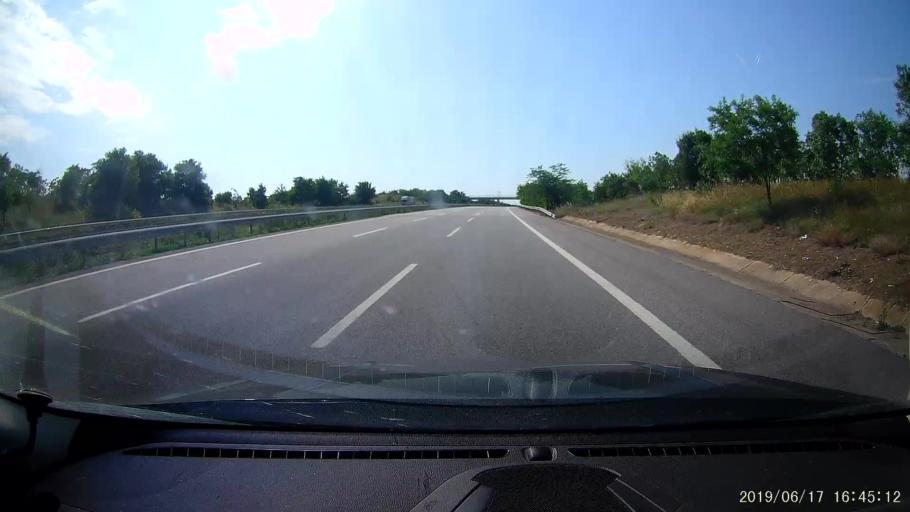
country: TR
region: Kirklareli
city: Luleburgaz
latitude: 41.4855
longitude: 27.2389
